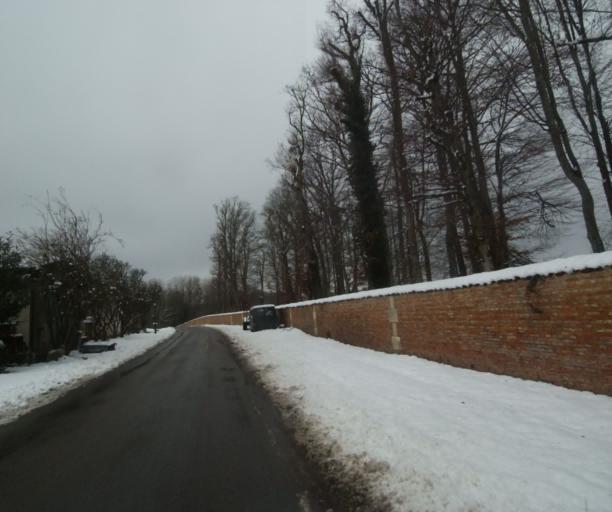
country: FR
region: Champagne-Ardenne
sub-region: Departement de la Haute-Marne
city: Laneuville-a-Remy
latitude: 48.4721
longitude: 4.8804
